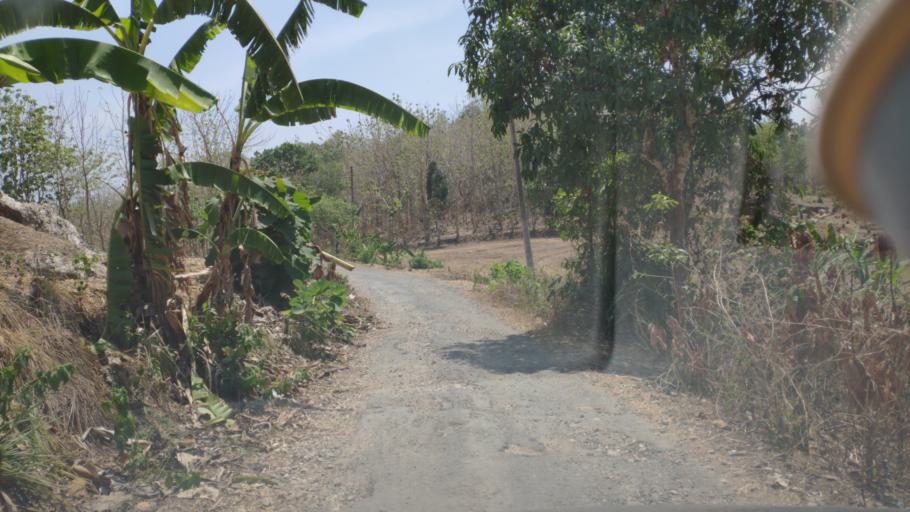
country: ID
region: Central Java
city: Guyangan
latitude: -6.9438
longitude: 111.1222
